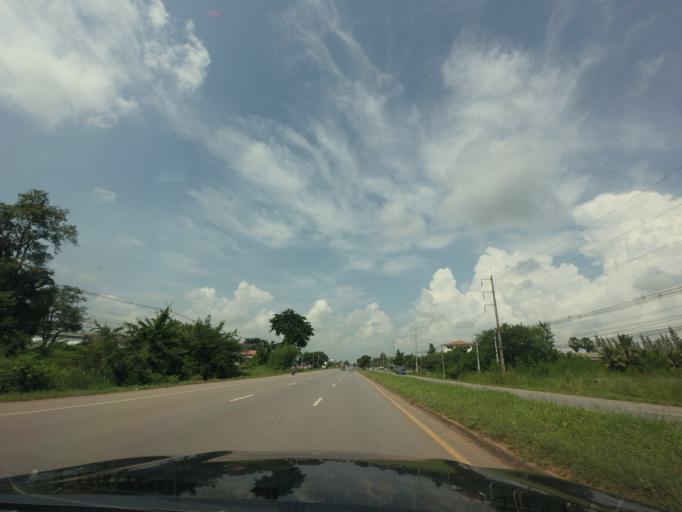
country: TH
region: Khon Kaen
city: Ban Fang
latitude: 16.4504
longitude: 102.7324
